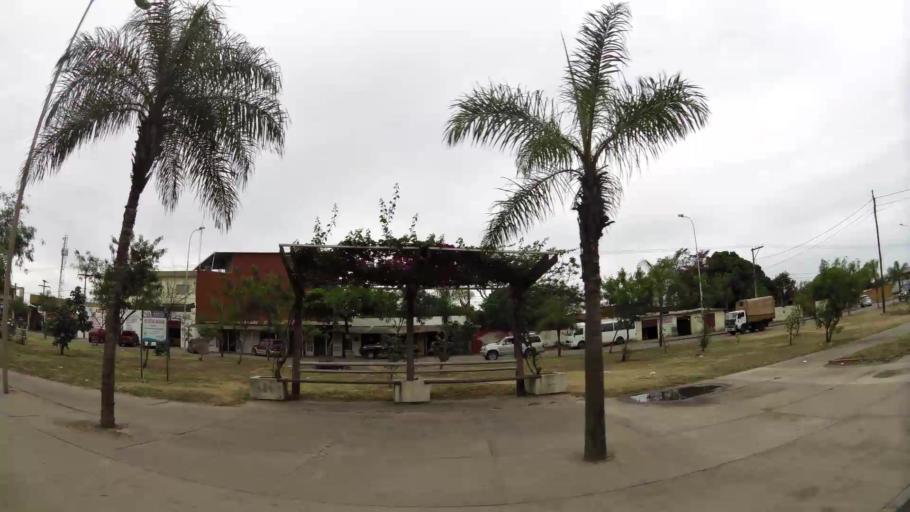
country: BO
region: Santa Cruz
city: Santa Cruz de la Sierra
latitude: -17.8199
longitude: -63.1970
